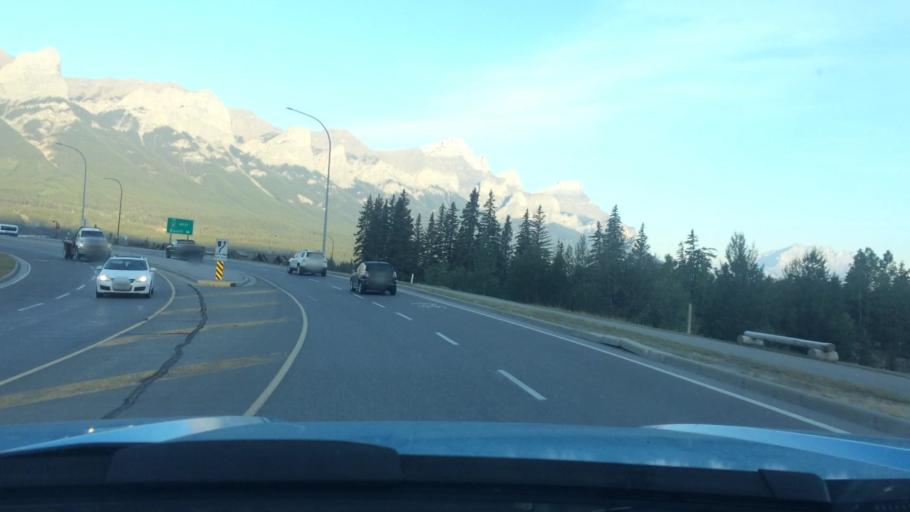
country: CA
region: Alberta
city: Canmore
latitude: 51.0904
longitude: -115.3407
